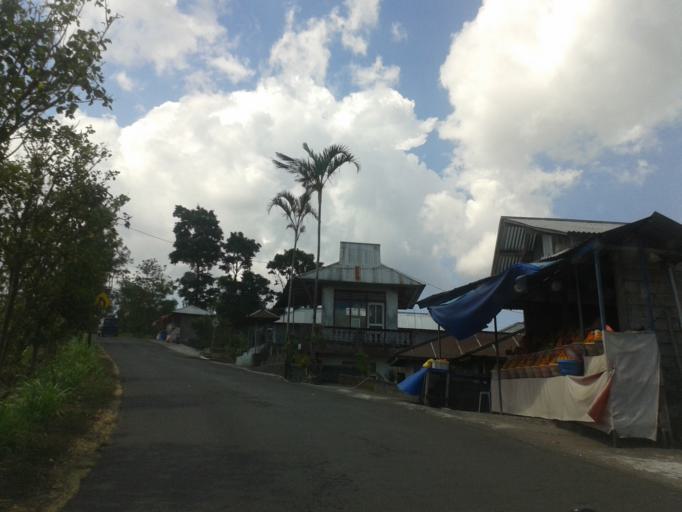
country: ID
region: Bali
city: Banjar Kedisan
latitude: -8.2812
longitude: 115.3507
